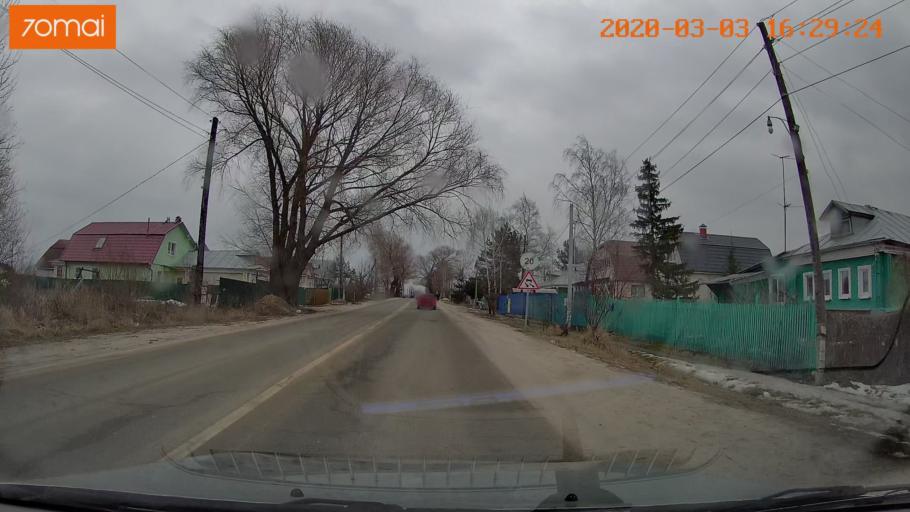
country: RU
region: Moskovskaya
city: Konobeyevo
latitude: 55.4369
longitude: 38.7003
